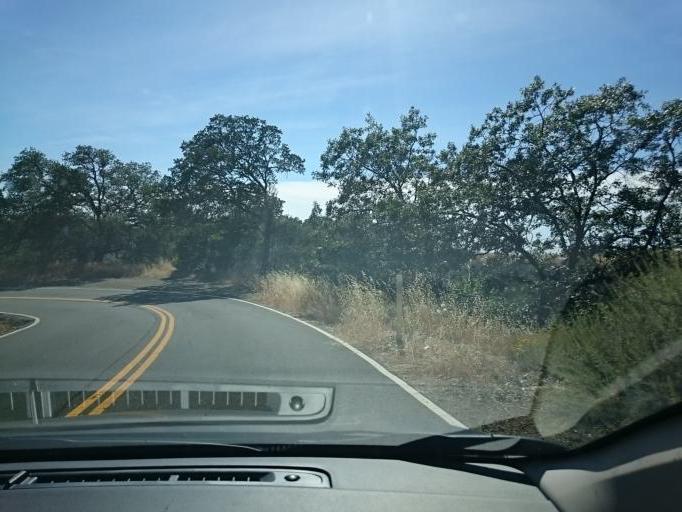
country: US
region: California
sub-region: Santa Clara County
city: East Foothills
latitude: 37.3371
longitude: -121.6669
